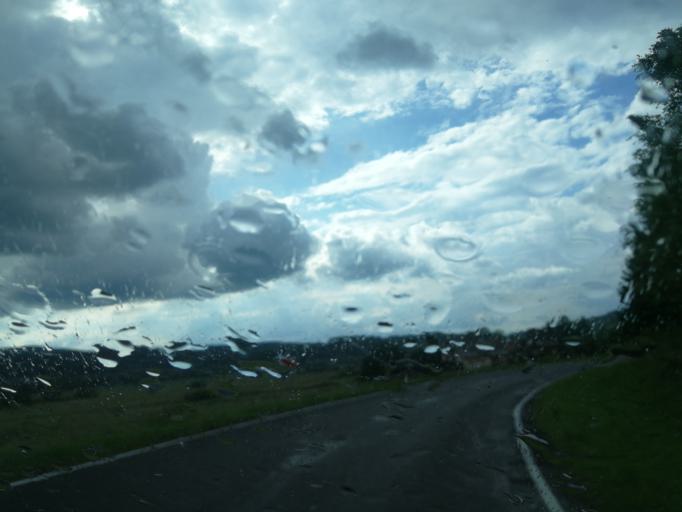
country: PL
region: Subcarpathian Voivodeship
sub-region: Powiat leski
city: Uherce Mineralne
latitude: 49.4577
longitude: 22.4106
